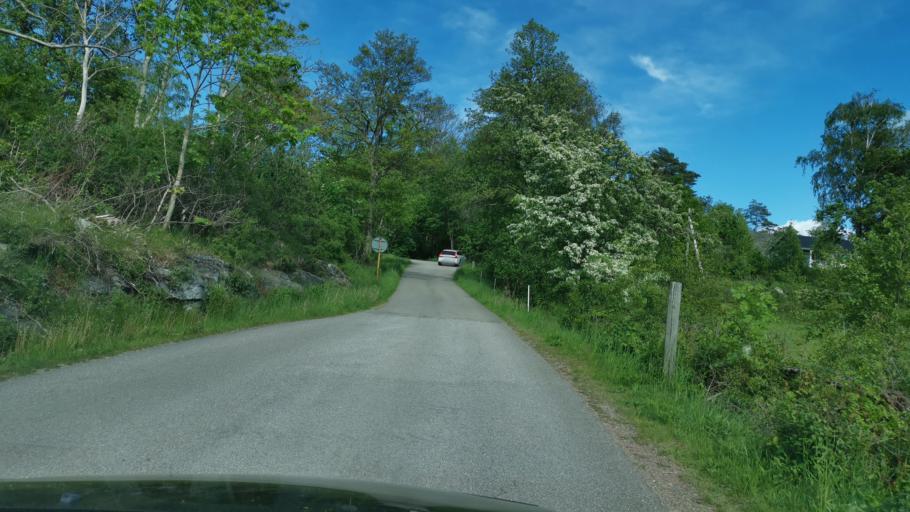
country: SE
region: Vaestra Goetaland
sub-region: Orust
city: Henan
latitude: 58.2661
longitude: 11.6060
